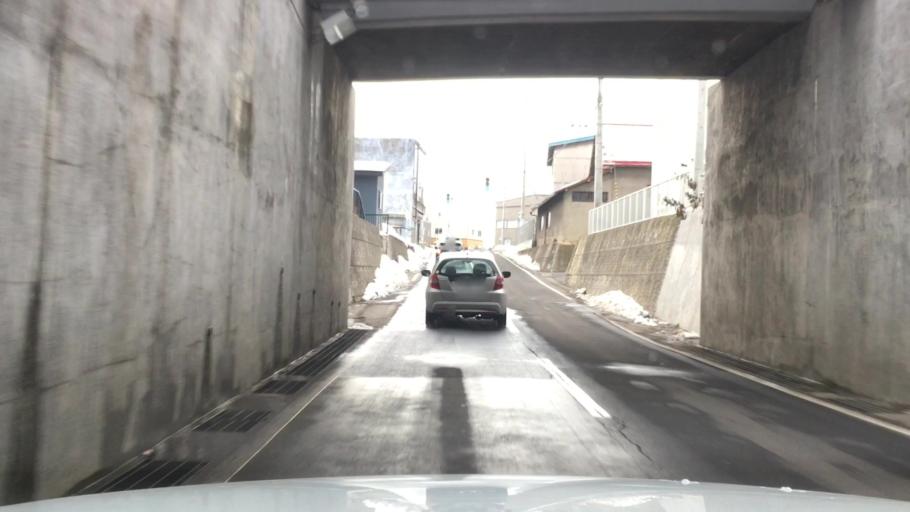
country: JP
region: Aomori
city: Hirosaki
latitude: 40.6035
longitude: 140.4834
